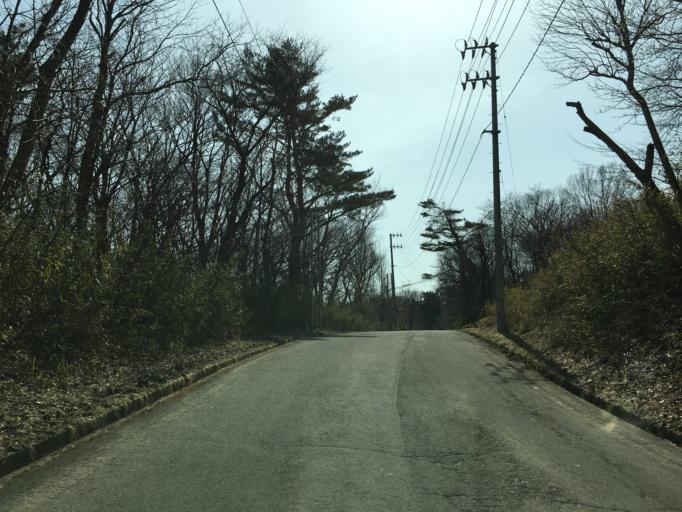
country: JP
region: Fukushima
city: Nihommatsu
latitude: 37.6379
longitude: 140.3580
